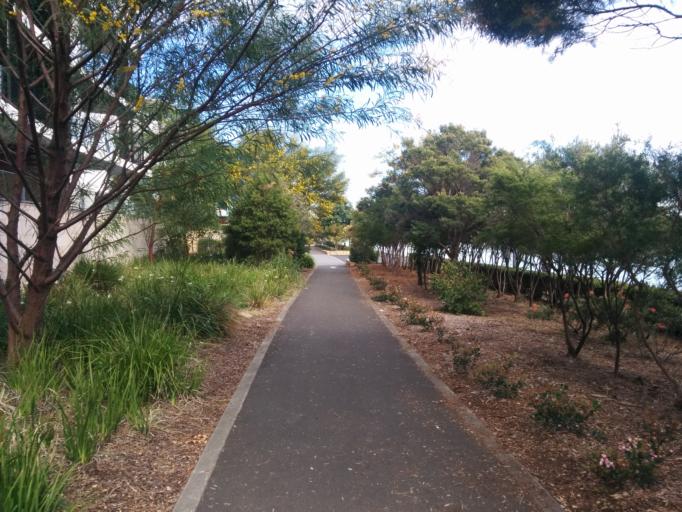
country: AU
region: New South Wales
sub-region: Canada Bay
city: Rhodes
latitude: -33.8316
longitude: 151.0834
